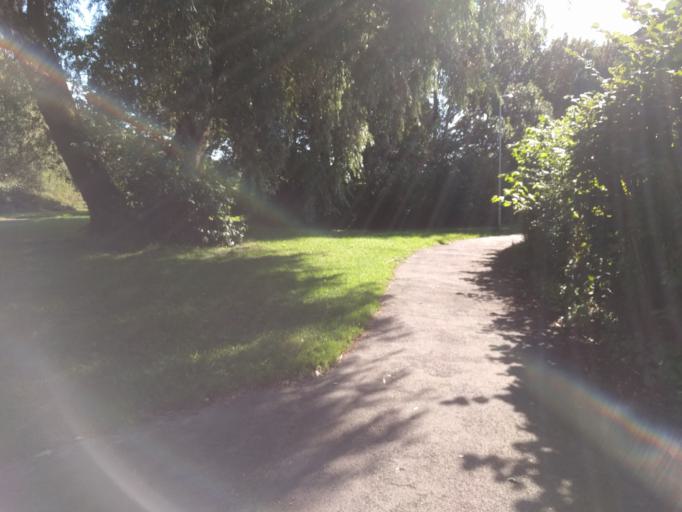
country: GB
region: England
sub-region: Warrington
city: Culcheth
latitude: 53.4232
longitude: -2.5115
